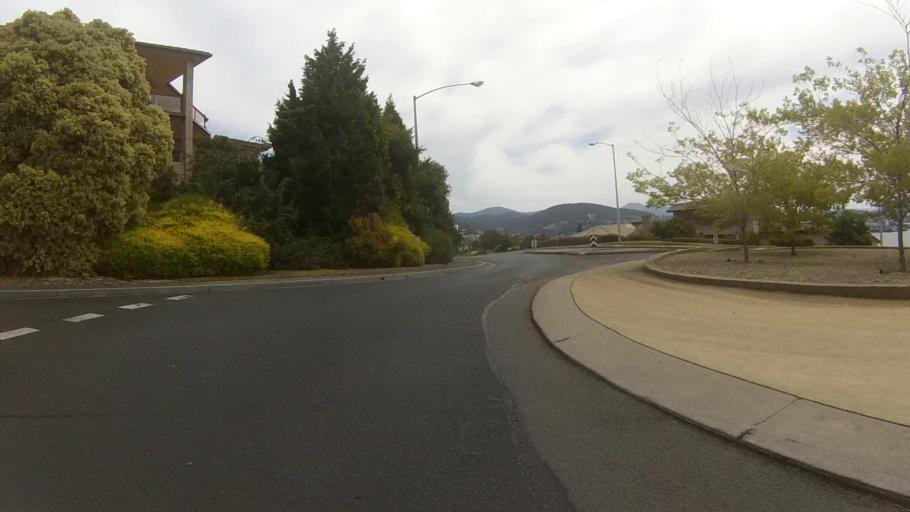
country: AU
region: Tasmania
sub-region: Kingborough
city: Taroona
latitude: -42.9179
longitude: 147.3490
